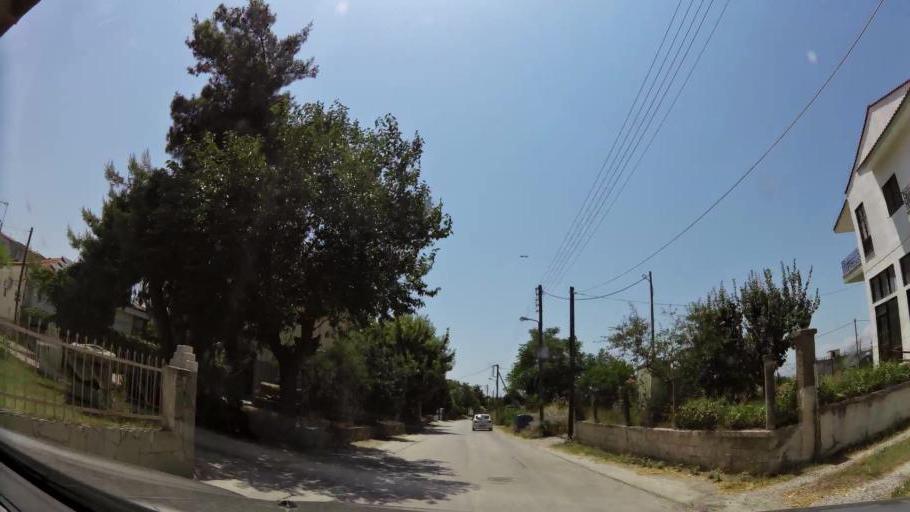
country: GR
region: Central Macedonia
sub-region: Nomos Thessalonikis
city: Epanomi
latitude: 40.4282
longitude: 22.9235
